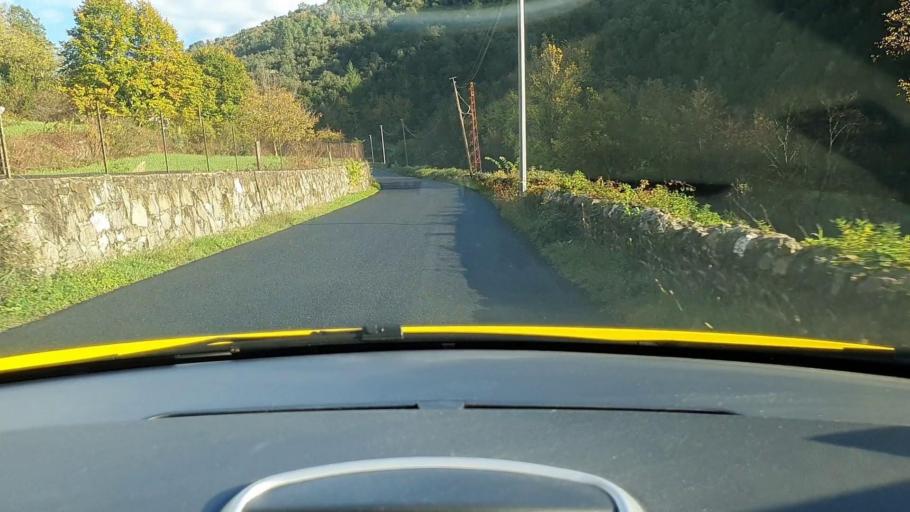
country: FR
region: Languedoc-Roussillon
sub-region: Departement du Gard
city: Sumene
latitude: 43.9901
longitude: 3.7126
